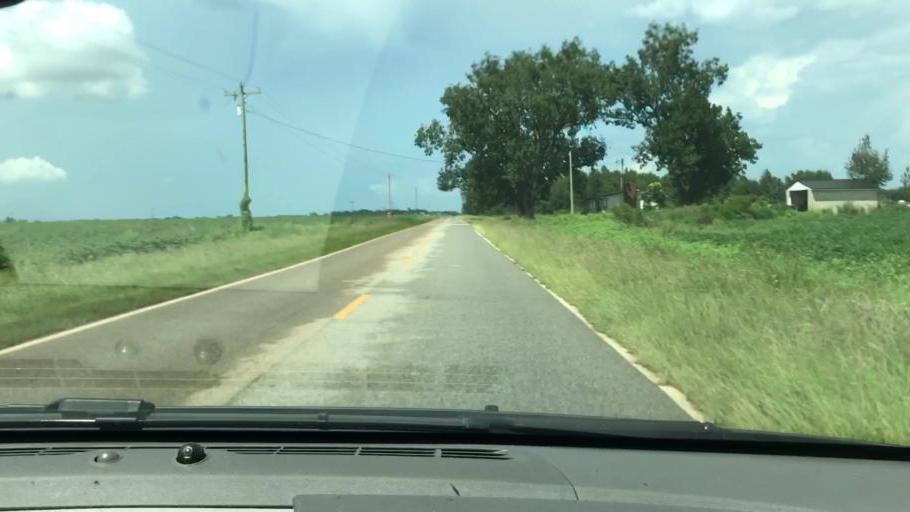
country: US
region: Georgia
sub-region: Seminole County
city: Donalsonville
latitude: 31.0948
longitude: -84.9962
